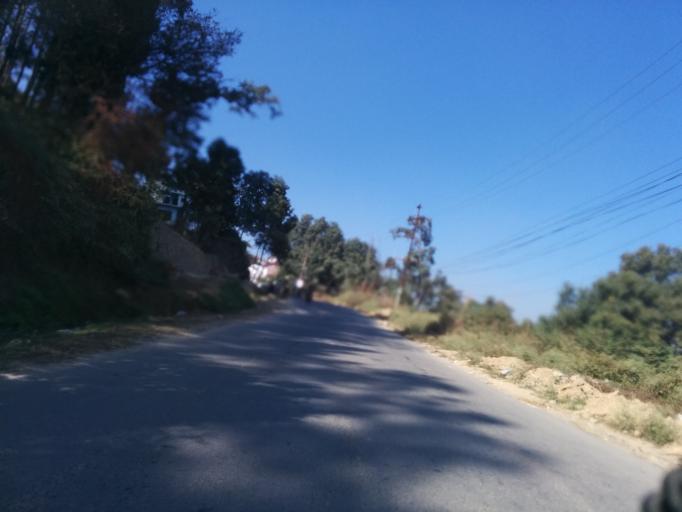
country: NP
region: Central Region
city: Kirtipur
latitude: 27.6816
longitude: 85.2750
